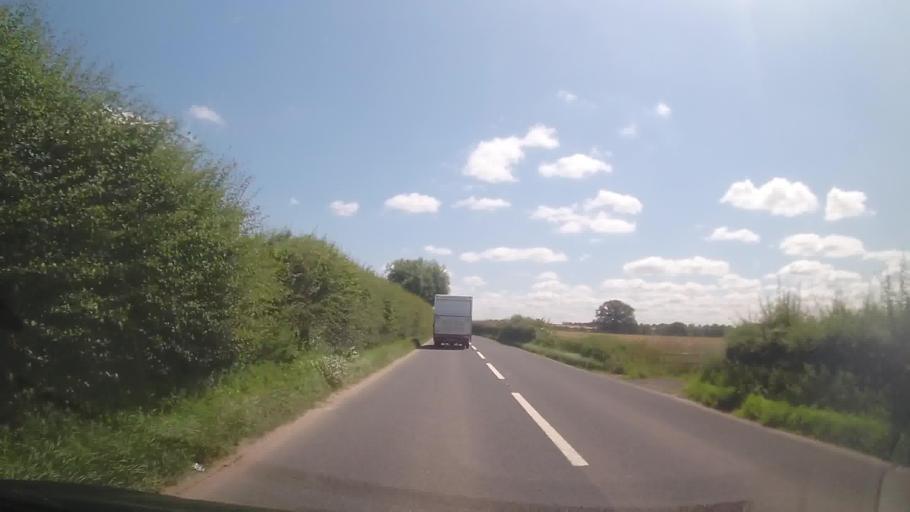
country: GB
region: England
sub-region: Herefordshire
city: Bodenham
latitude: 52.1469
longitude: -2.6386
